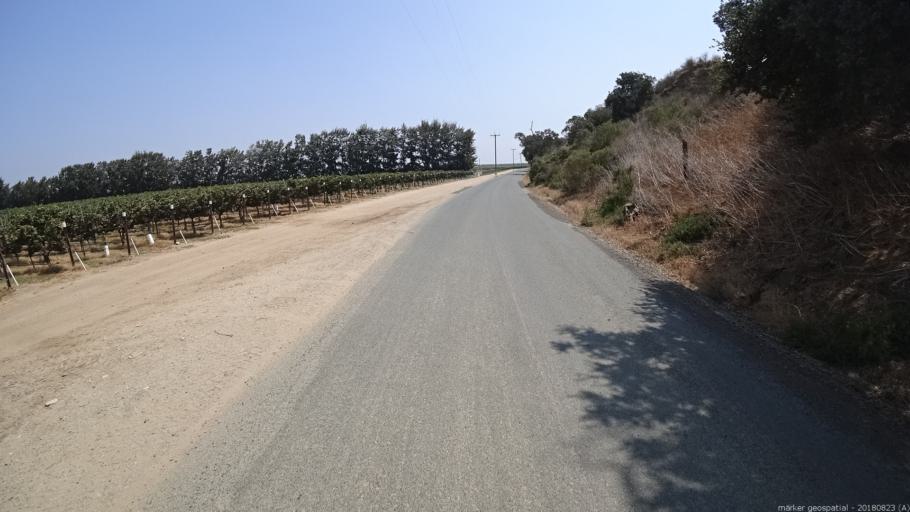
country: US
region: California
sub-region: Monterey County
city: Soledad
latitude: 36.3654
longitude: -121.3105
